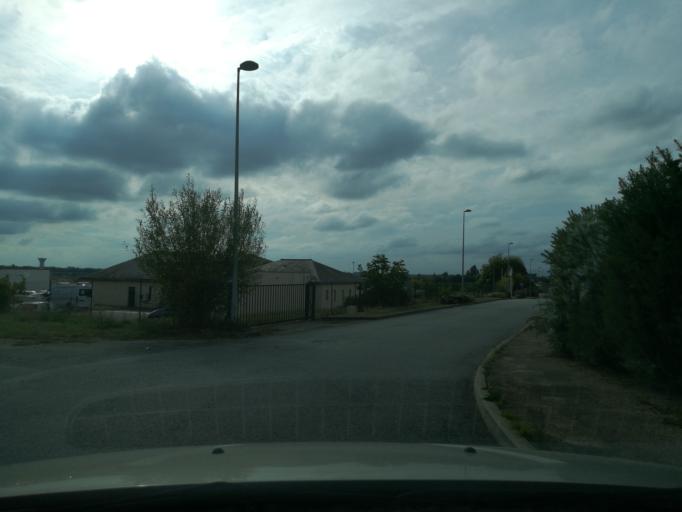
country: FR
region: Brittany
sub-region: Departement d'Ille-et-Vilaine
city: Montauban-de-Bretagne
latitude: 48.1957
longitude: -2.0327
